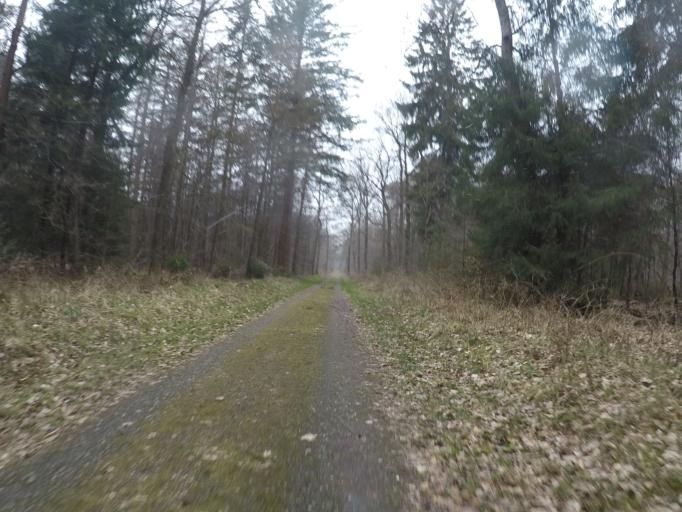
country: DE
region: Lower Saxony
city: Drangstedt
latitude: 53.6220
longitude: 8.7077
